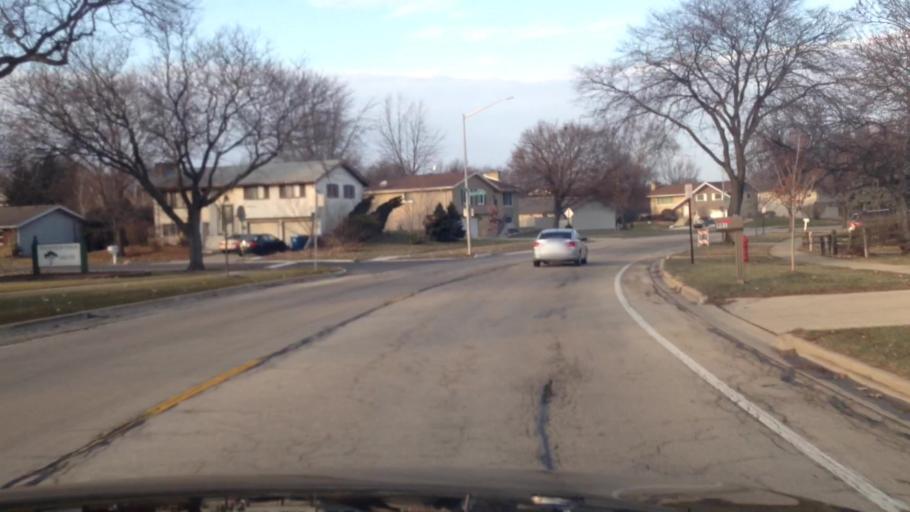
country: US
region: Illinois
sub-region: Cook County
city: Schaumburg
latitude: 42.0094
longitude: -88.1024
